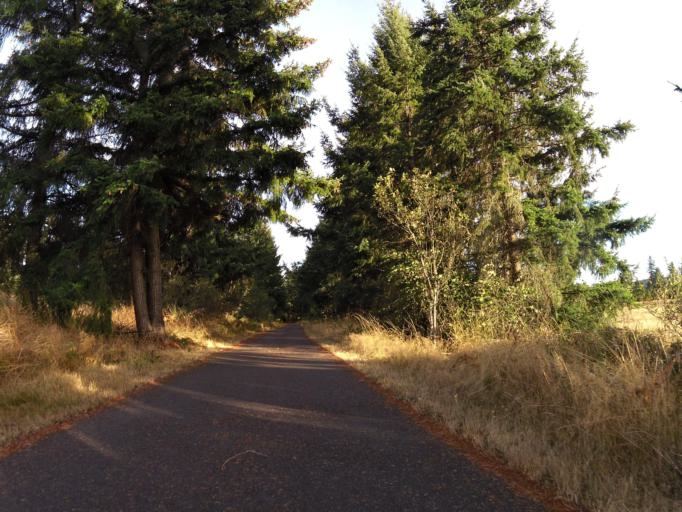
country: US
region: Washington
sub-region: Thurston County
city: Rainier
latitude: 46.8773
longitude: -122.7309
